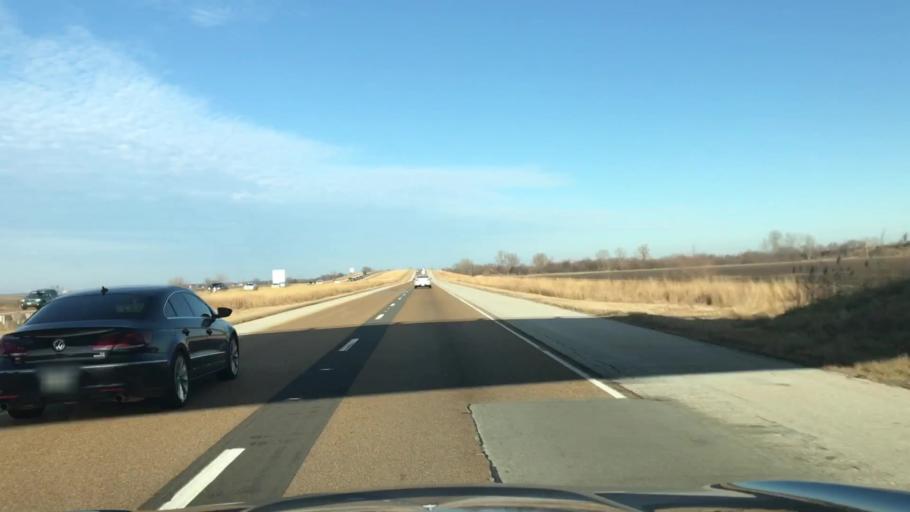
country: US
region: Illinois
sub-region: Montgomery County
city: Litchfield
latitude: 39.1903
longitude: -89.6705
